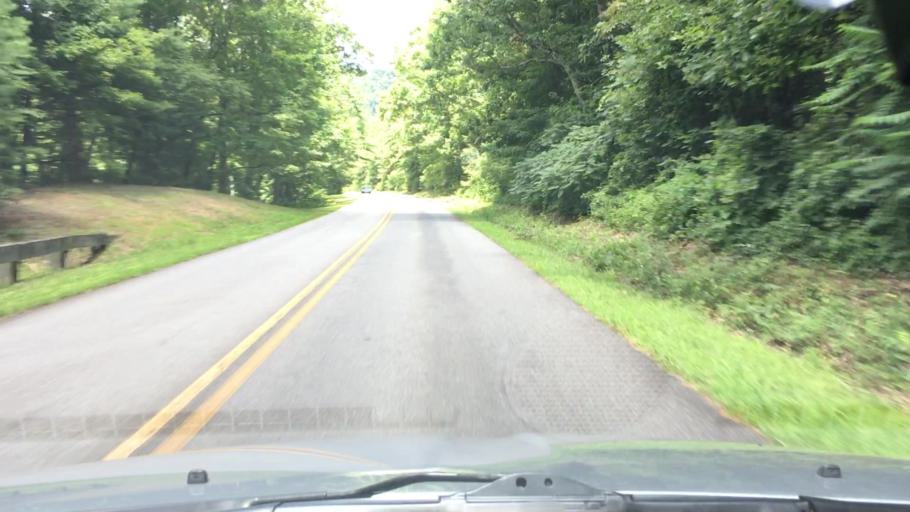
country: US
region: North Carolina
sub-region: Buncombe County
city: Asheville
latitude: 35.6258
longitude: -82.4923
